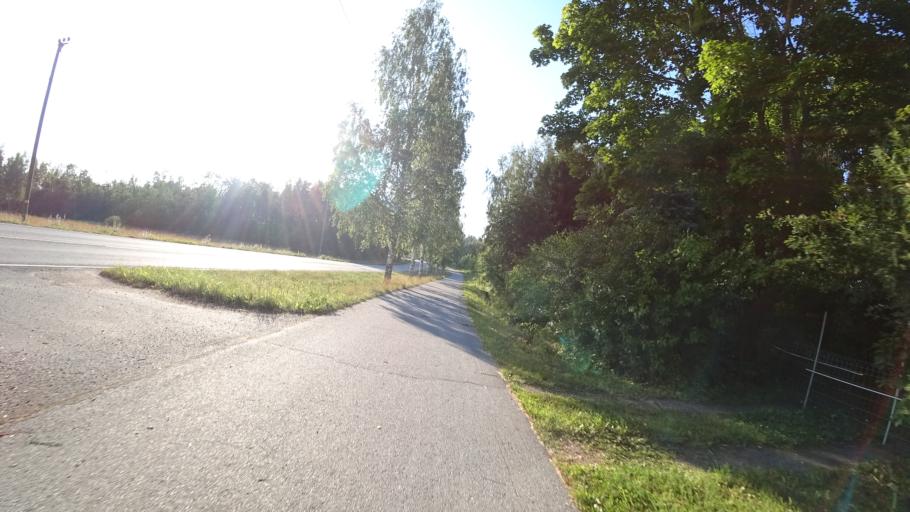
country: FI
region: Pirkanmaa
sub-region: Tampere
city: Nokia
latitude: 61.4685
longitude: 23.3965
